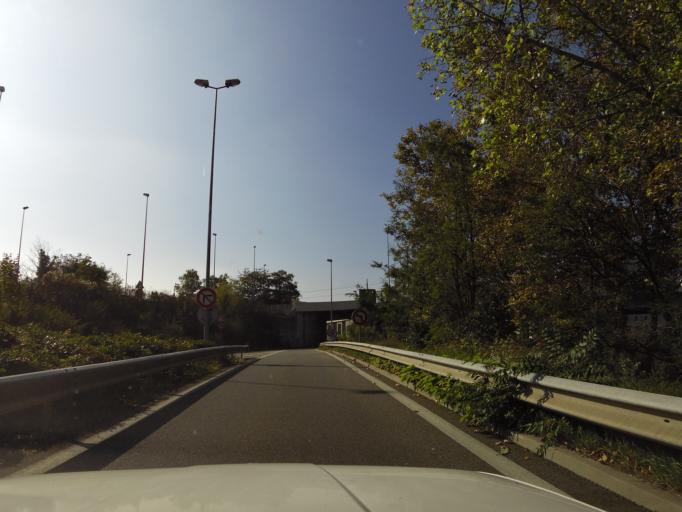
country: FR
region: Rhone-Alpes
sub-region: Departement du Rhone
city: Caluire-et-Cuire
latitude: 45.7892
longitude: 4.8621
